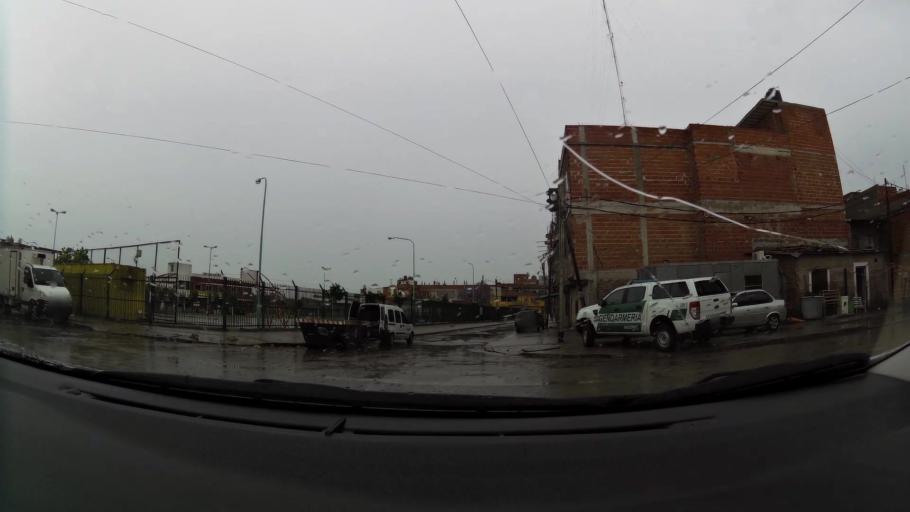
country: AR
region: Buenos Aires F.D.
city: Villa Lugano
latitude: -34.6646
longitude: -58.4558
